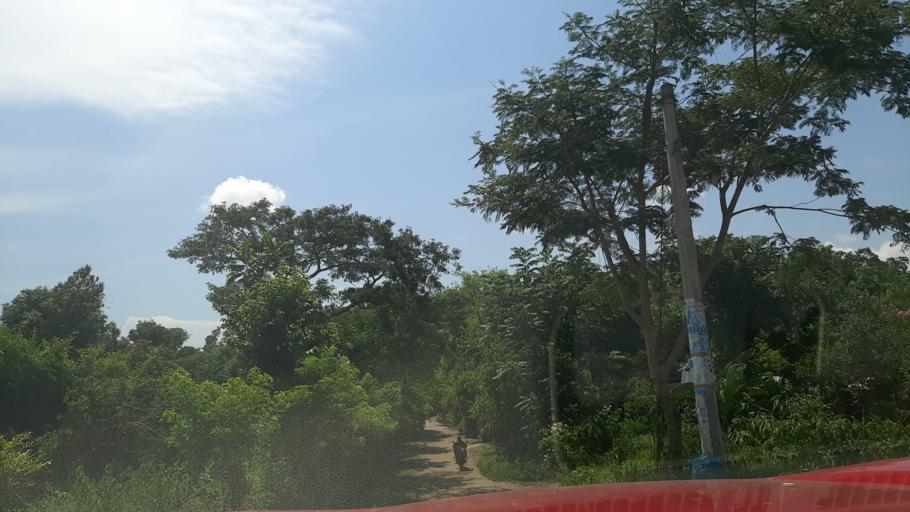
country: MX
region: Veracruz
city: Cazones de Herrera
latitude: 20.6780
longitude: -97.3229
